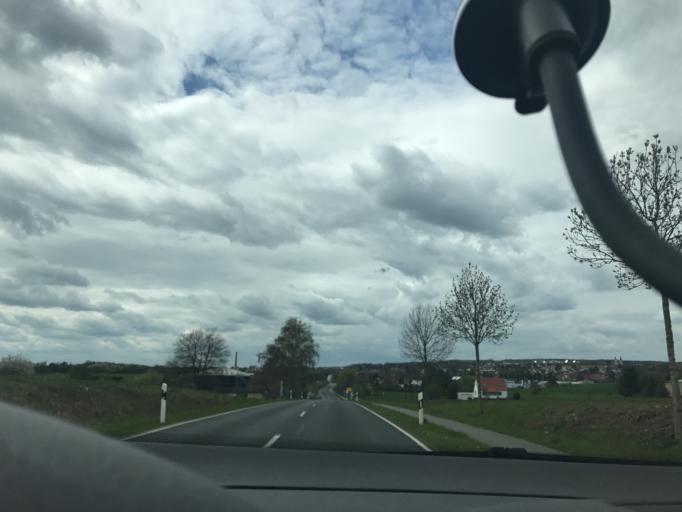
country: DE
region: Lower Saxony
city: Schoningen
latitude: 52.1290
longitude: 10.9827
